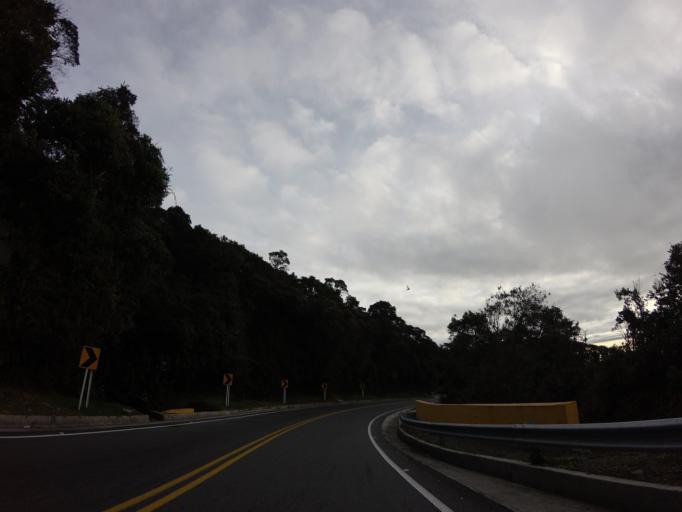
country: CO
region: Tolima
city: Herveo
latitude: 5.0891
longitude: -75.2797
